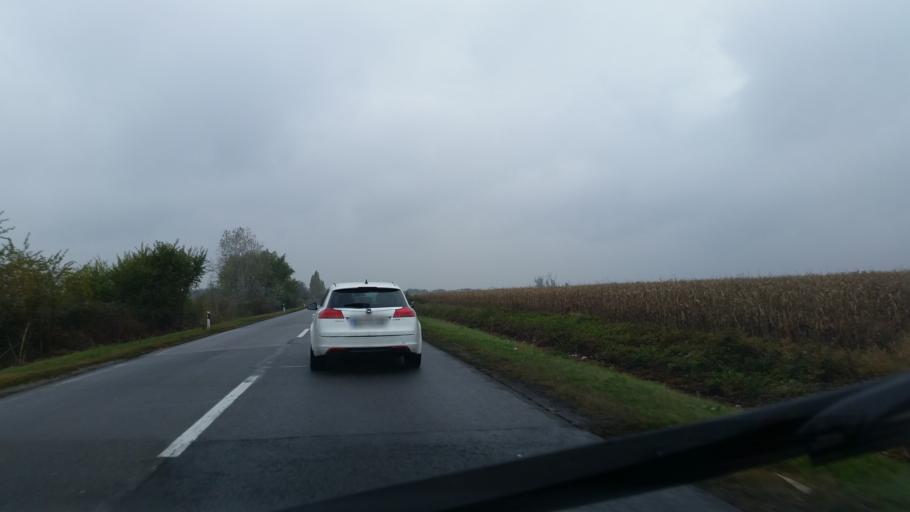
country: RS
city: Sefkerin
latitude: 44.9379
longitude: 20.4361
